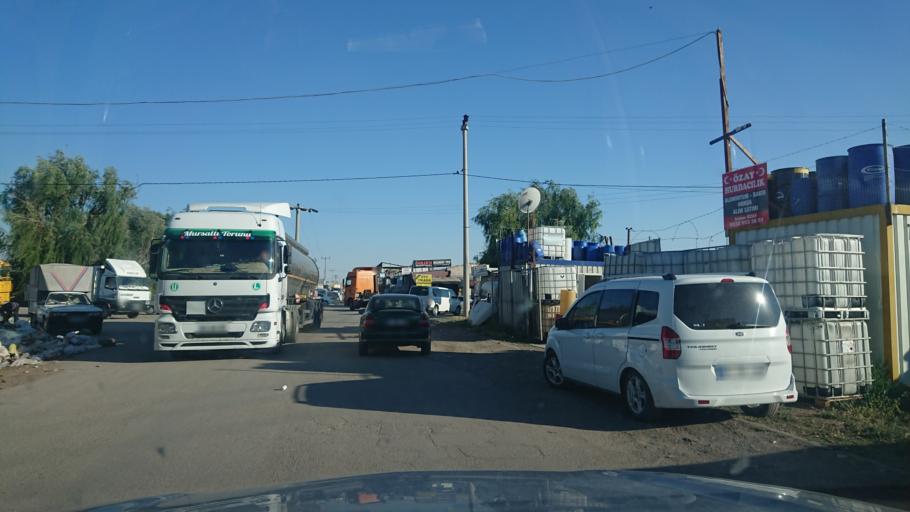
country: TR
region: Aksaray
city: Aksaray
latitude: 38.3746
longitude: 33.9919
